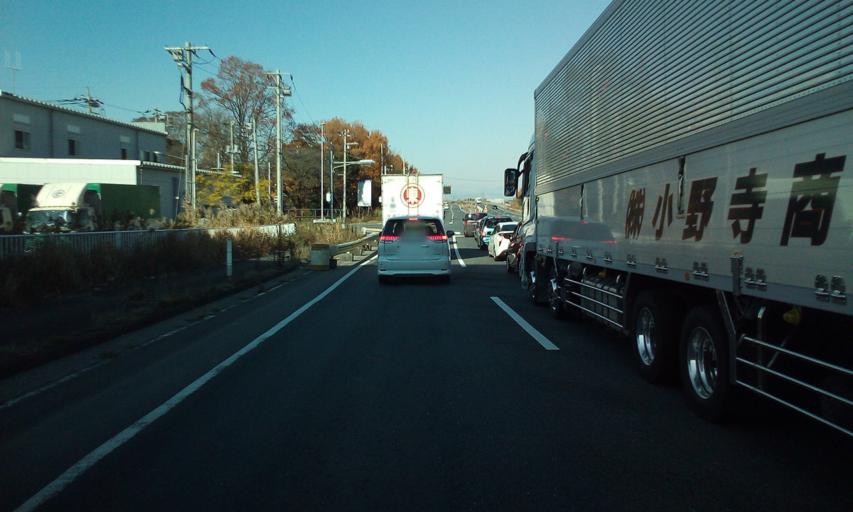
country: JP
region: Ibaraki
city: Sakai
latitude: 36.0825
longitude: 139.7686
